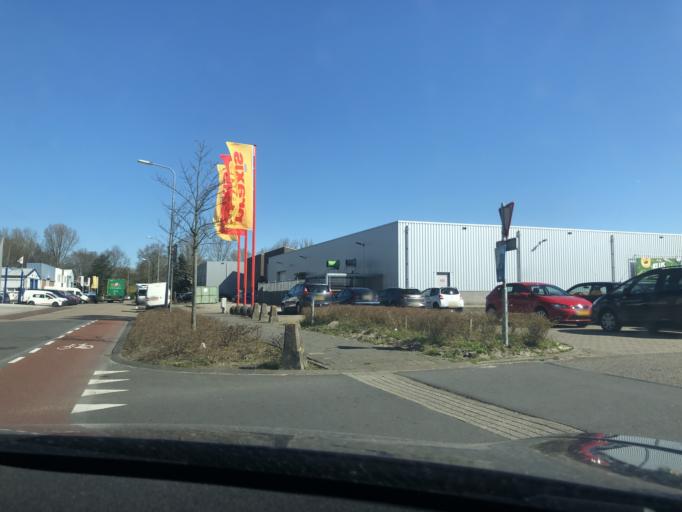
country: NL
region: Zeeland
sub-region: Gemeente Vlissingen
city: Vlissingen
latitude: 51.4562
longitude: 3.5852
